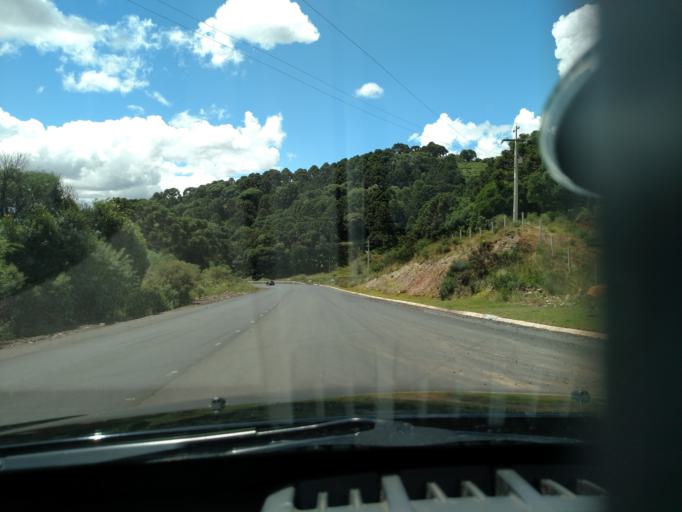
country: BR
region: Santa Catarina
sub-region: Sao Joaquim
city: Sao Joaquim
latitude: -28.2766
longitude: -49.9567
